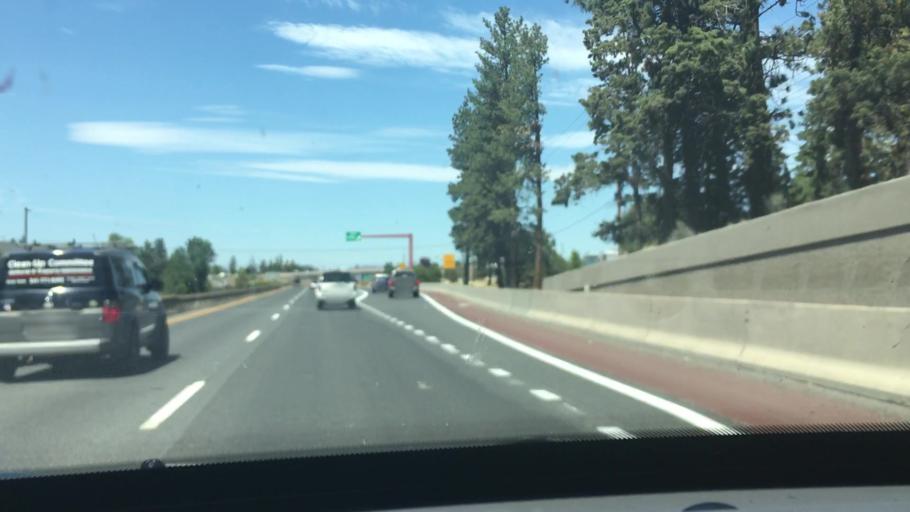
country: US
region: Oregon
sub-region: Deschutes County
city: Bend
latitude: 44.0864
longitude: -121.3007
